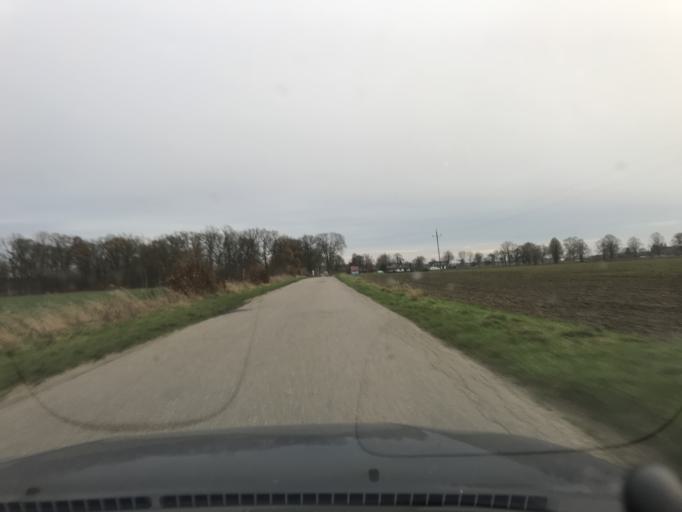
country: PL
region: Pomeranian Voivodeship
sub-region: Powiat slupski
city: Kobylnica
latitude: 54.4515
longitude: 16.8804
